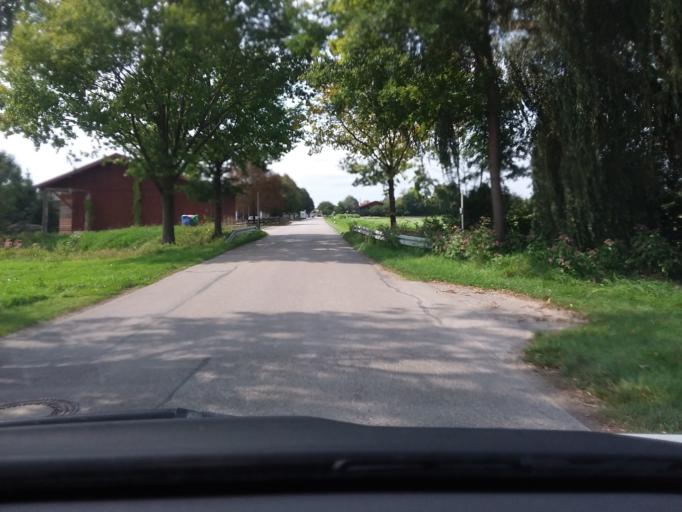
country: DE
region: Bavaria
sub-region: Upper Bavaria
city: Ismaning
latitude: 48.2299
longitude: 11.7057
